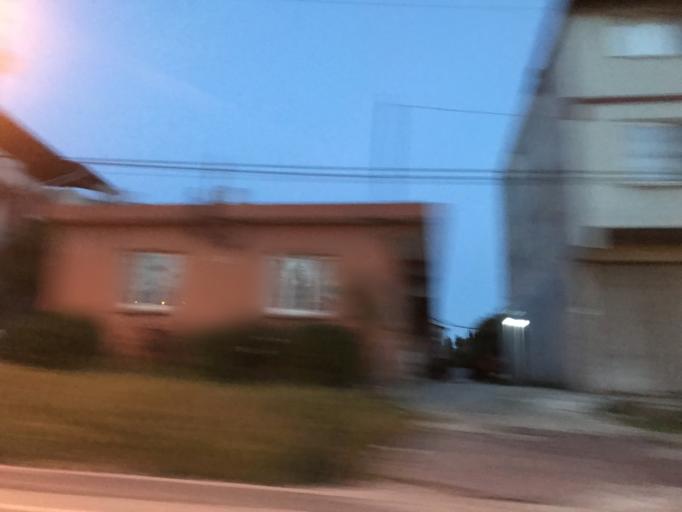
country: TR
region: Hatay
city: Asagiokcular
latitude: 36.1748
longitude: 36.1146
